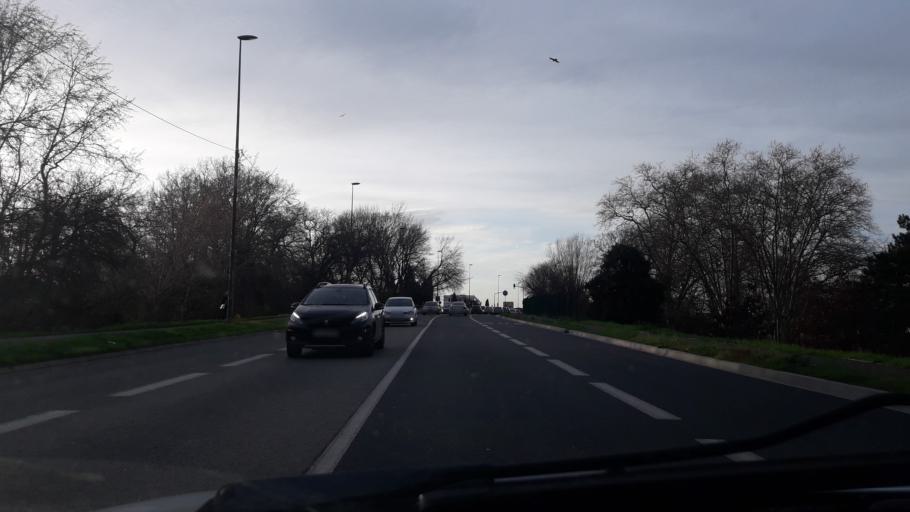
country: FR
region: Midi-Pyrenees
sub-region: Departement de la Haute-Garonne
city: Portet-sur-Garonne
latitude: 43.5593
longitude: 1.3971
